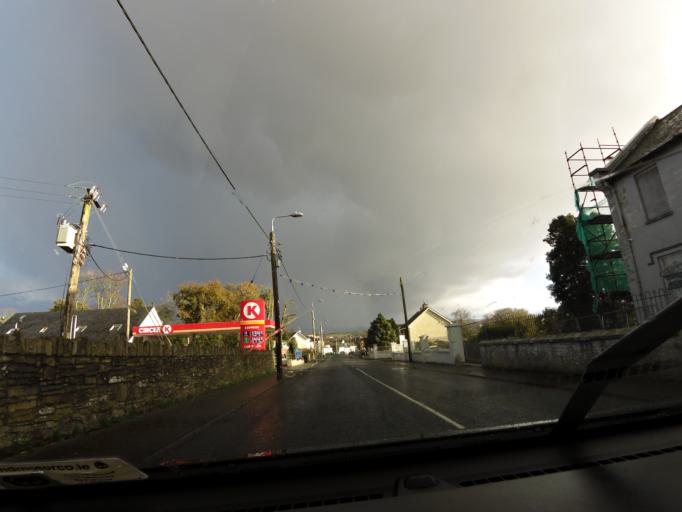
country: IE
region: Munster
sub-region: North Tipperary
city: Newport
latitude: 52.7122
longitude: -8.4106
